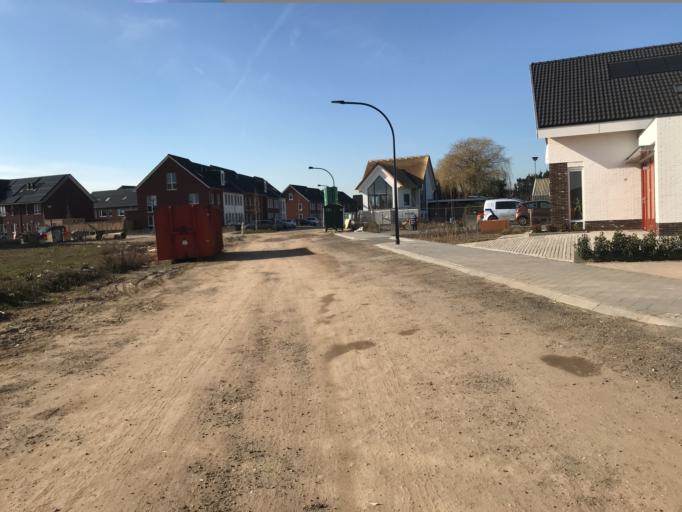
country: NL
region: Gelderland
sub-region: Gemeente Arnhem
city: Arnhem
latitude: 51.9412
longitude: 5.9257
